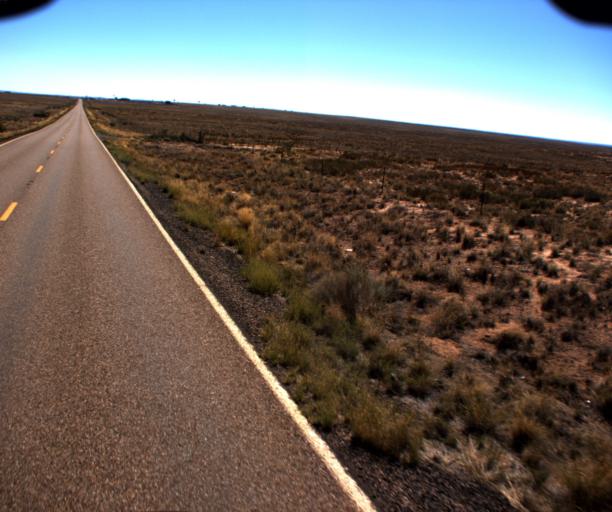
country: US
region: Arizona
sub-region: Navajo County
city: Holbrook
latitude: 34.9970
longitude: -110.0893
